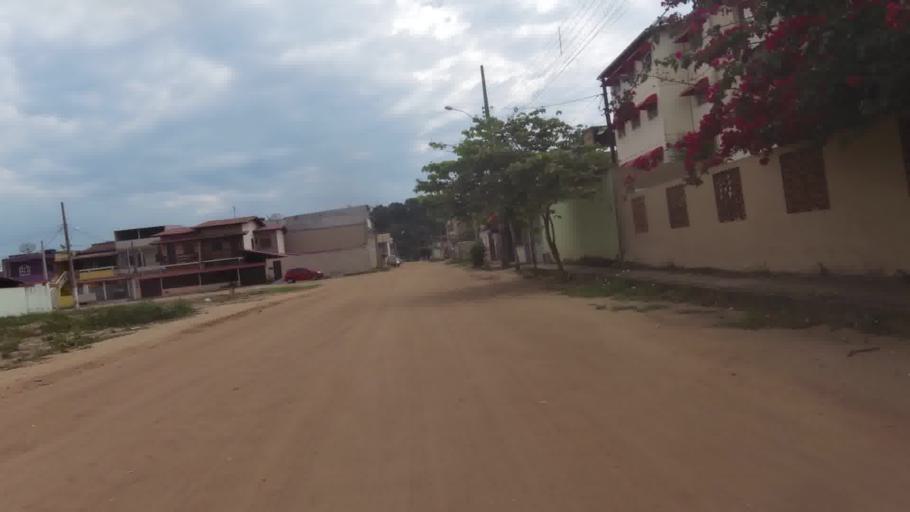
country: BR
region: Espirito Santo
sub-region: Piuma
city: Piuma
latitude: -20.8422
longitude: -40.7386
